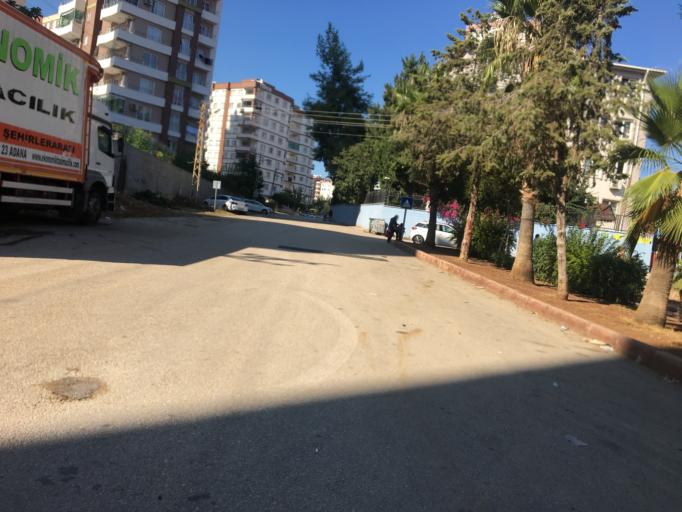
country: TR
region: Adana
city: Seyhan
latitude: 37.0296
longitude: 35.2864
